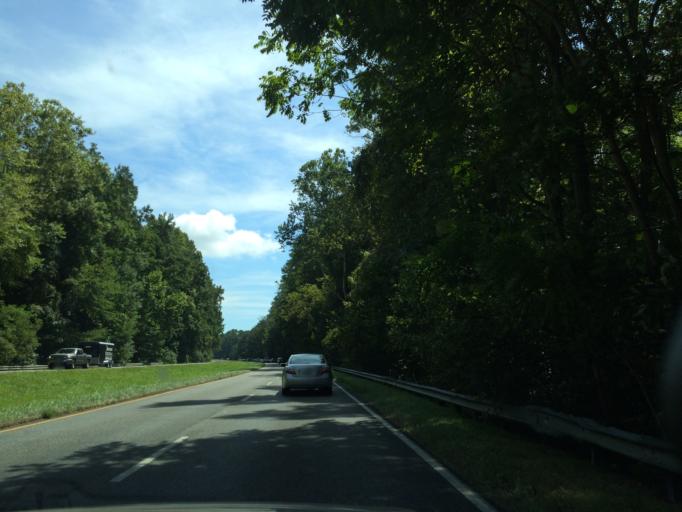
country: US
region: Virginia
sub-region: York County
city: Yorktown
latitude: 37.2086
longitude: -76.5109
